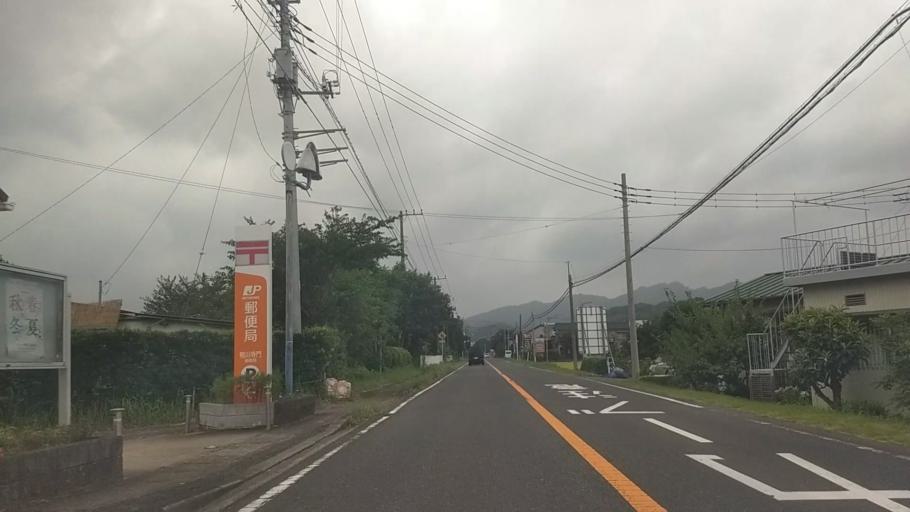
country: JP
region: Chiba
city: Kawaguchi
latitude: 35.1336
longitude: 140.0061
